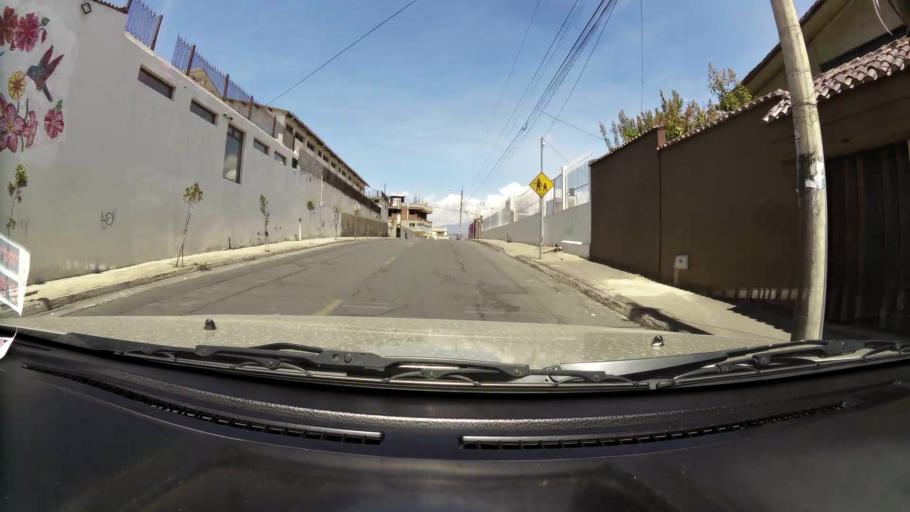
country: EC
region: Chimborazo
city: Riobamba
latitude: -1.6624
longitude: -78.6565
